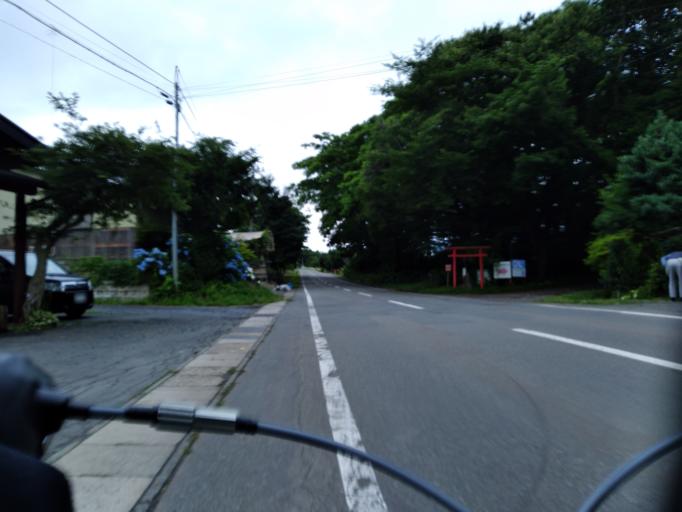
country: JP
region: Iwate
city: Morioka-shi
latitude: 39.8034
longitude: 141.0987
